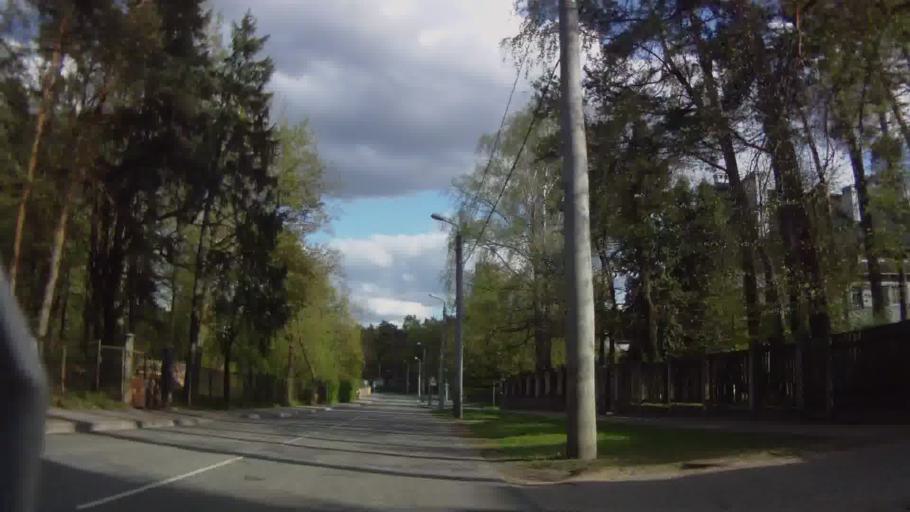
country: LV
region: Riga
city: Jaunciems
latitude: 57.0047
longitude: 24.1675
